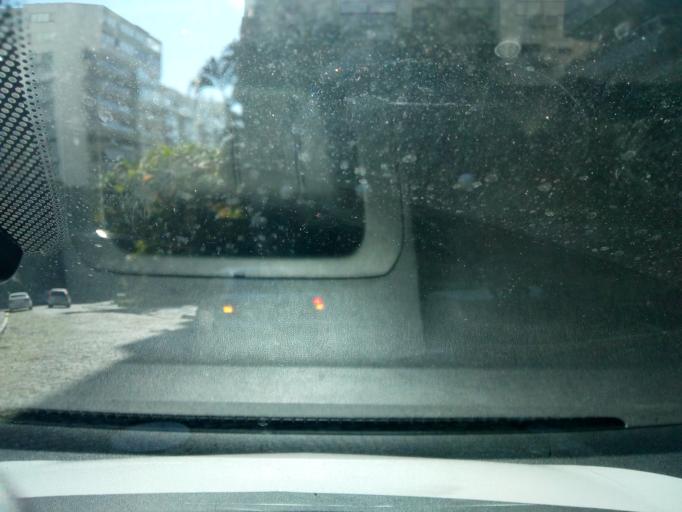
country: BR
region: Rio de Janeiro
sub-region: Rio De Janeiro
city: Rio de Janeiro
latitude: -22.9860
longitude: -43.2356
